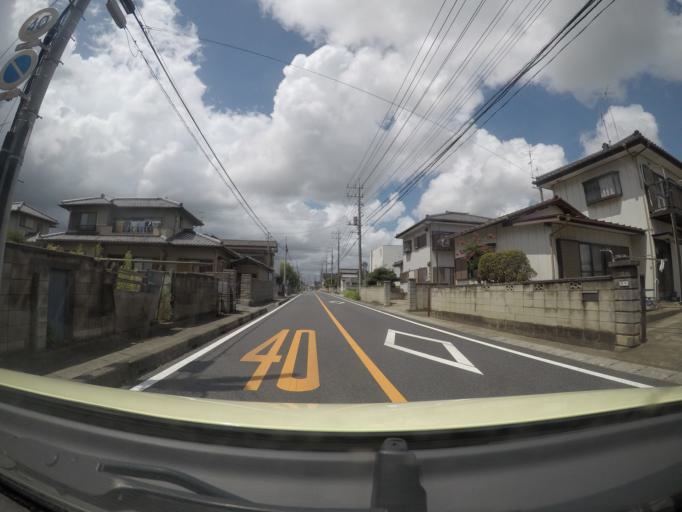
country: JP
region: Ibaraki
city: Mitsukaido
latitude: 36.0300
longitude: 139.9903
